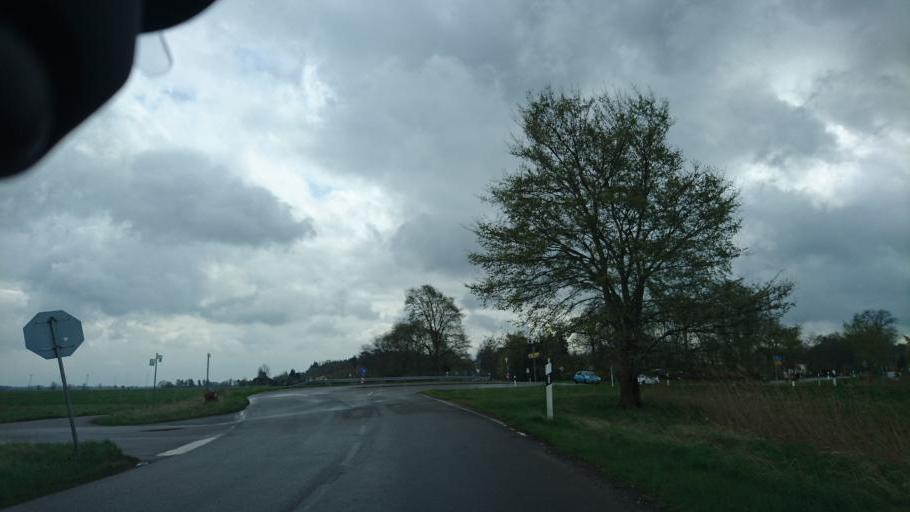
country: DE
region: Mecklenburg-Vorpommern
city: Bad Sulze
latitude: 54.1024
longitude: 12.6751
